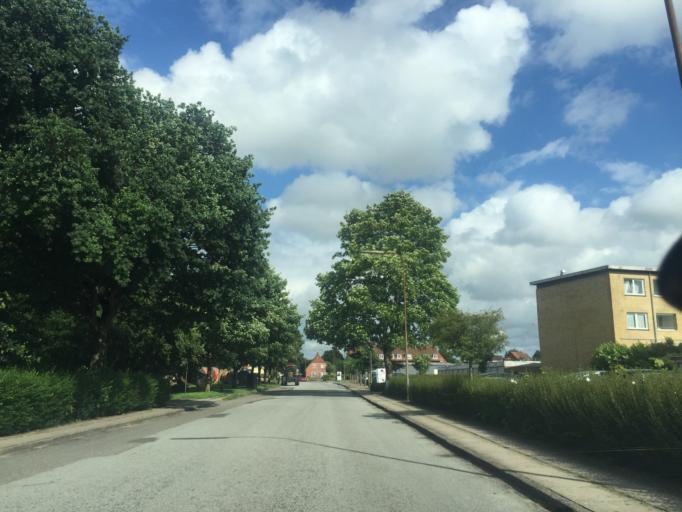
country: DK
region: South Denmark
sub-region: Odense Kommune
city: Odense
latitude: 55.3596
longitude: 10.3872
